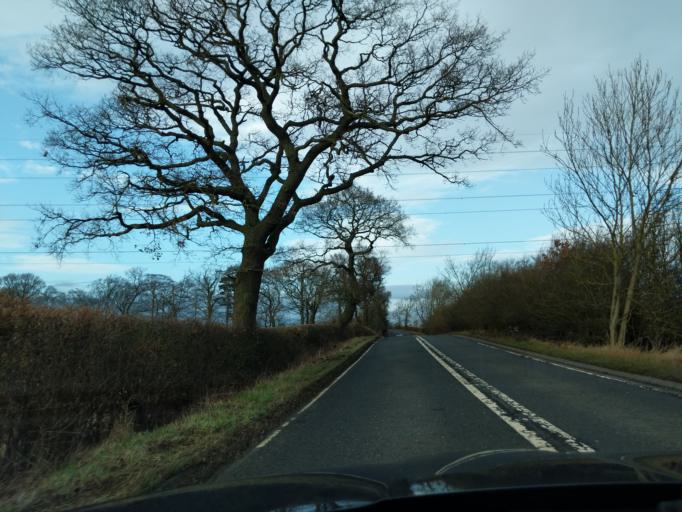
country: GB
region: England
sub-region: Northumberland
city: Darras Hall
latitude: 55.0583
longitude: -1.7690
